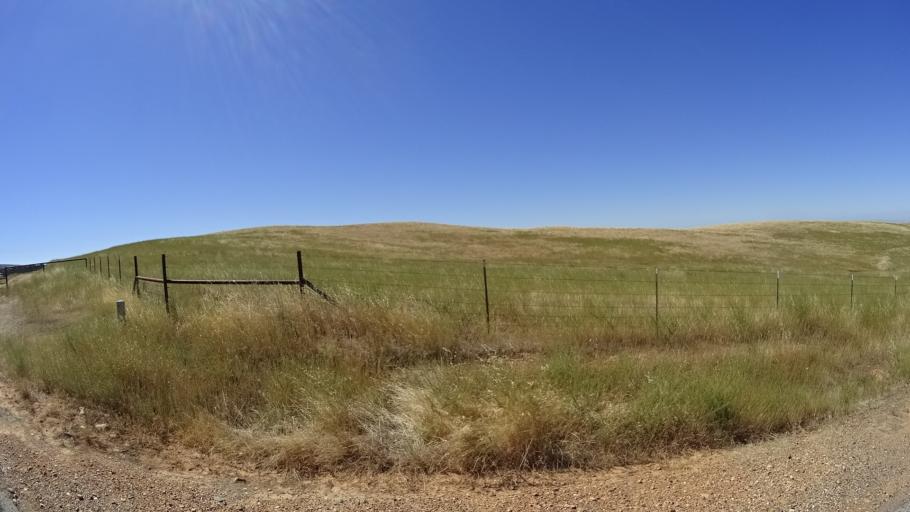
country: US
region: California
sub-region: Calaveras County
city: Rancho Calaveras
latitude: 38.0153
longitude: -120.8179
